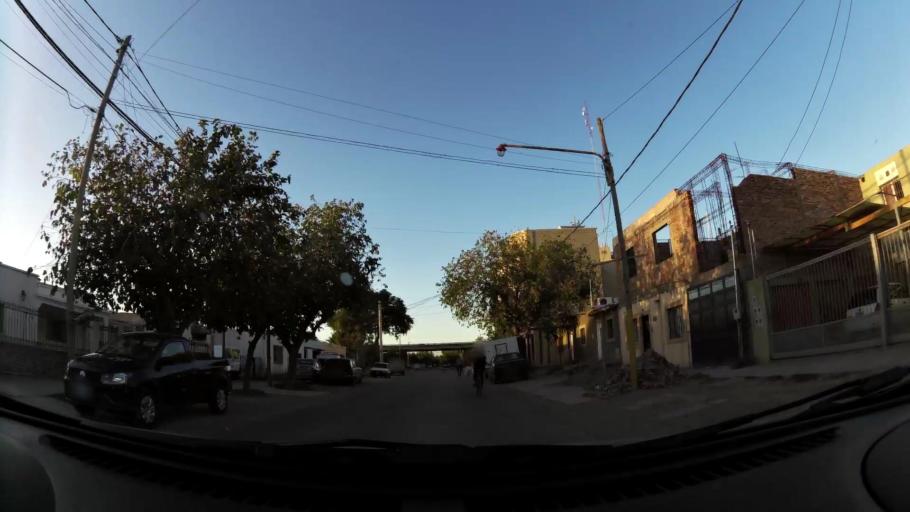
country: AR
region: San Juan
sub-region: Departamento de Santa Lucia
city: Santa Lucia
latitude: -31.5180
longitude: -68.5099
